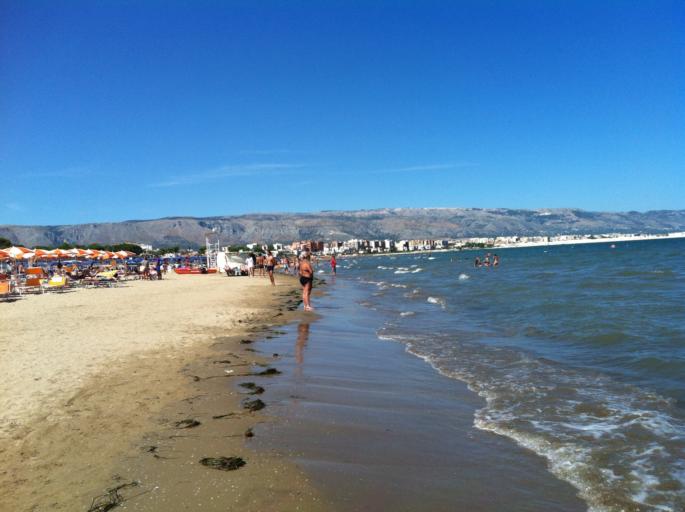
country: IT
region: Apulia
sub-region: Provincia di Foggia
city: Manfredonia
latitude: 41.6083
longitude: 15.8987
